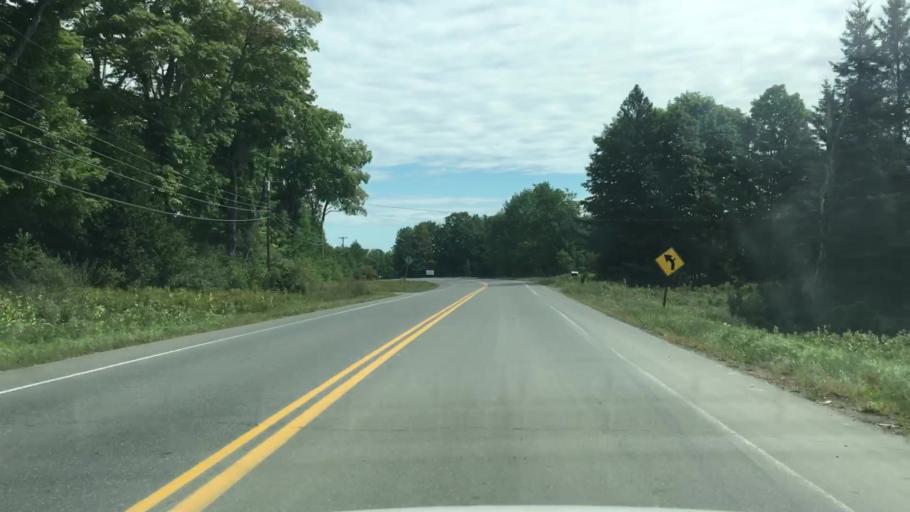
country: US
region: Maine
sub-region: Piscataquis County
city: Dover-Foxcroft
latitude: 45.2016
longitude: -69.1918
